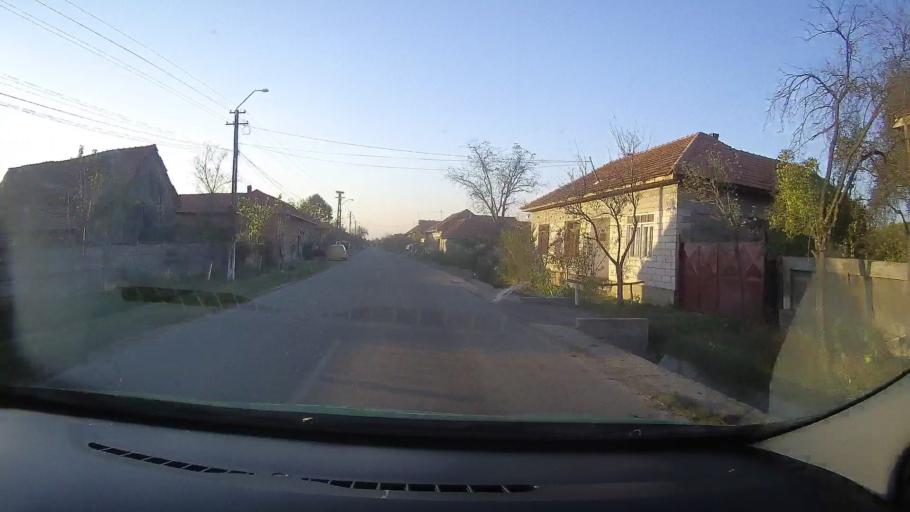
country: RO
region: Timis
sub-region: Comuna Traian Vuia
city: Traian Vuia
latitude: 45.7929
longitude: 22.0718
